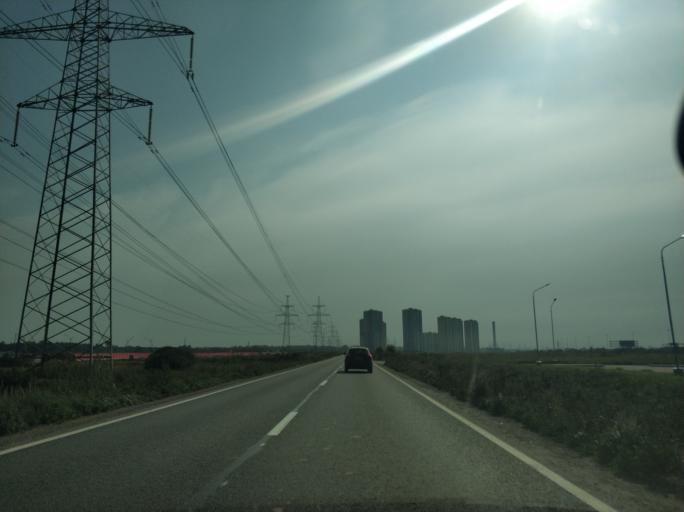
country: RU
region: Leningrad
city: Murino
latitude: 60.0185
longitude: 30.4692
